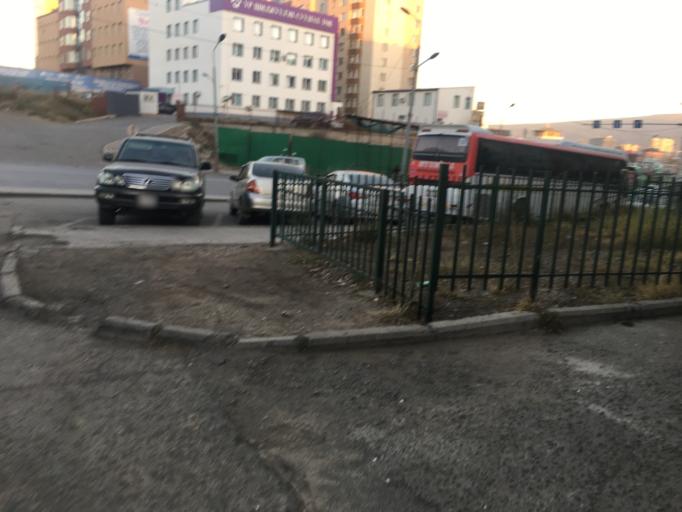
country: MN
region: Ulaanbaatar
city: Ulaanbaatar
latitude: 47.9248
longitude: 106.8881
